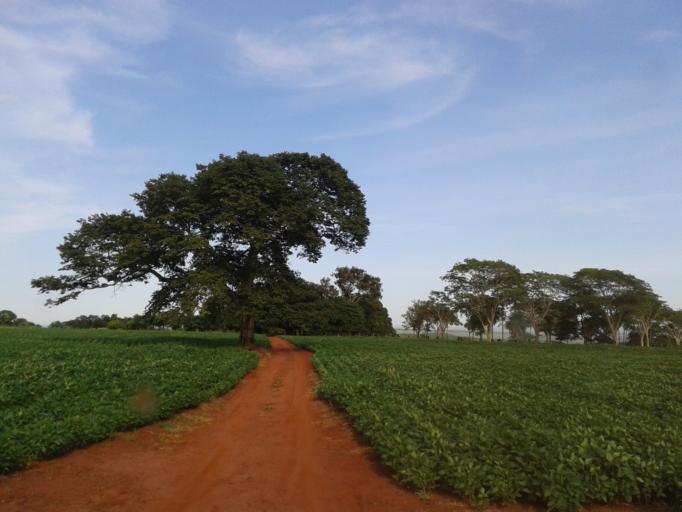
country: BR
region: Minas Gerais
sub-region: Centralina
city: Centralina
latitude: -18.7132
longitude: -49.1891
